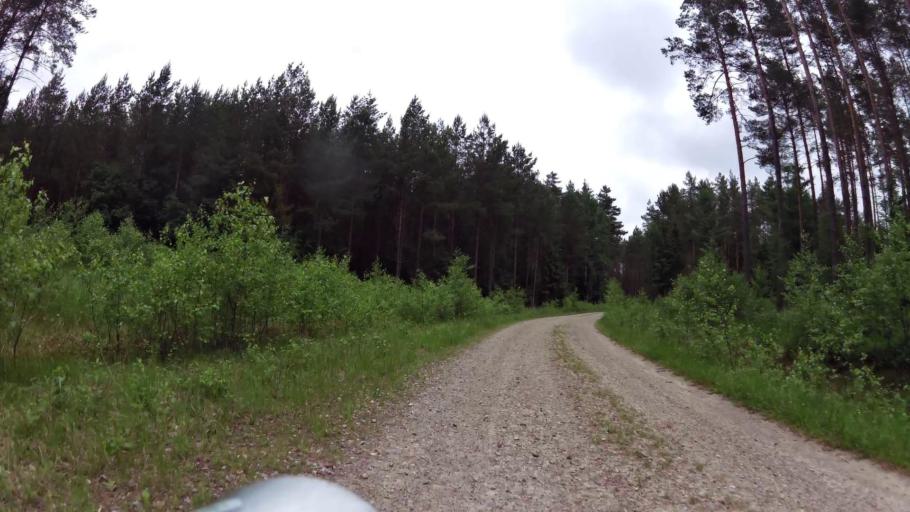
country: PL
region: West Pomeranian Voivodeship
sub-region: Powiat szczecinecki
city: Bialy Bor
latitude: 53.9180
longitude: 16.8304
